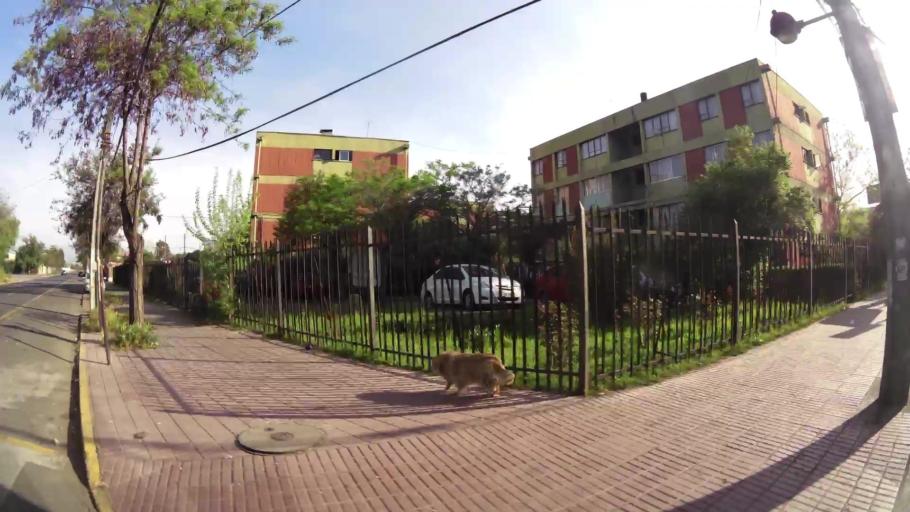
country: CL
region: Santiago Metropolitan
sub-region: Provincia de Santiago
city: Santiago
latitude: -33.5079
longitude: -70.6241
